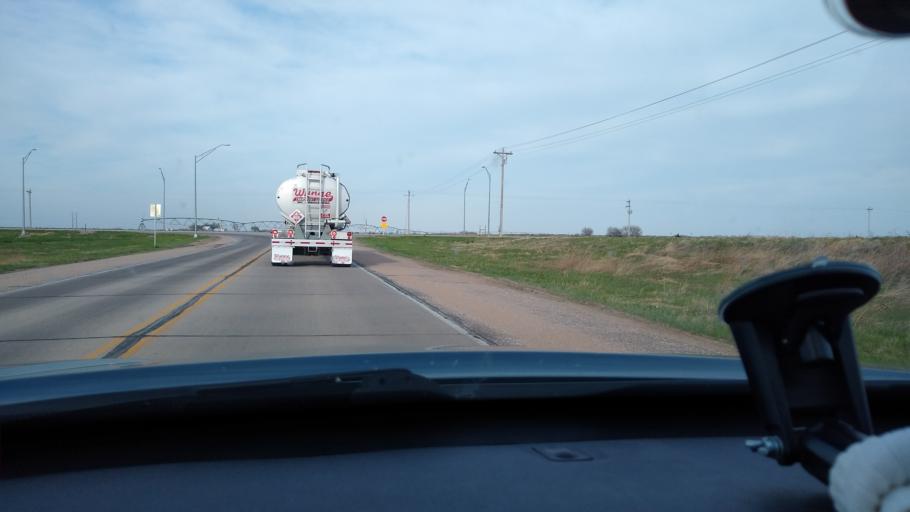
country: US
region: Nebraska
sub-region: Fillmore County
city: Geneva
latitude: 40.5561
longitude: -97.5935
